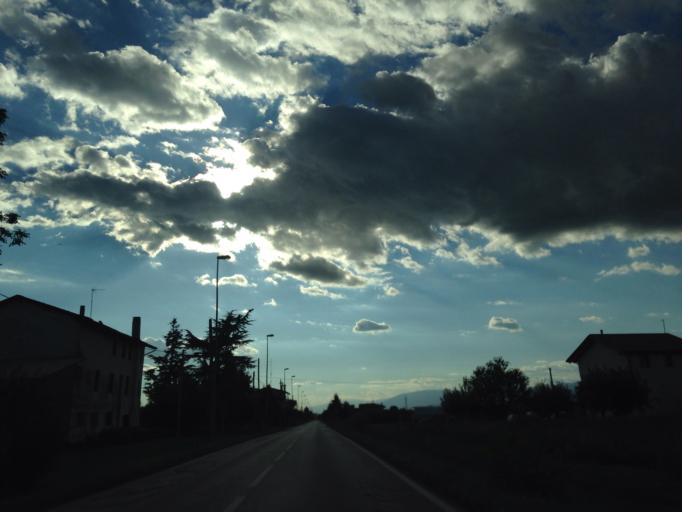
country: IT
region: Friuli Venezia Giulia
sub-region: Provincia di Pordenone
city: Sacile
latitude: 45.9528
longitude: 12.5344
